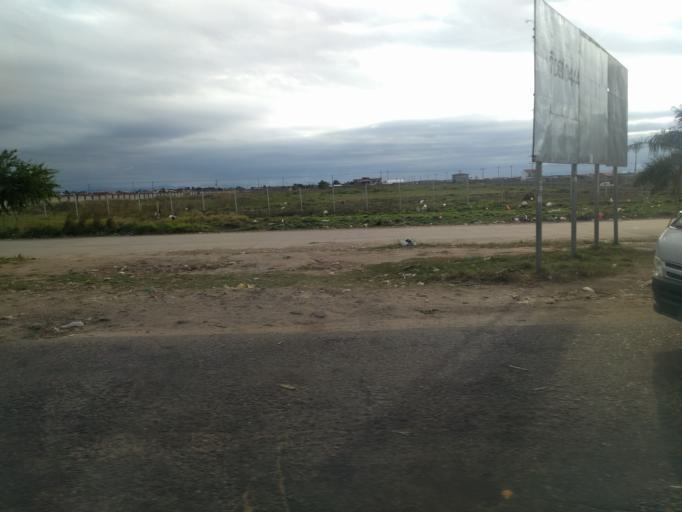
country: BO
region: Santa Cruz
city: La Belgica
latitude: -17.6037
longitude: -63.1592
